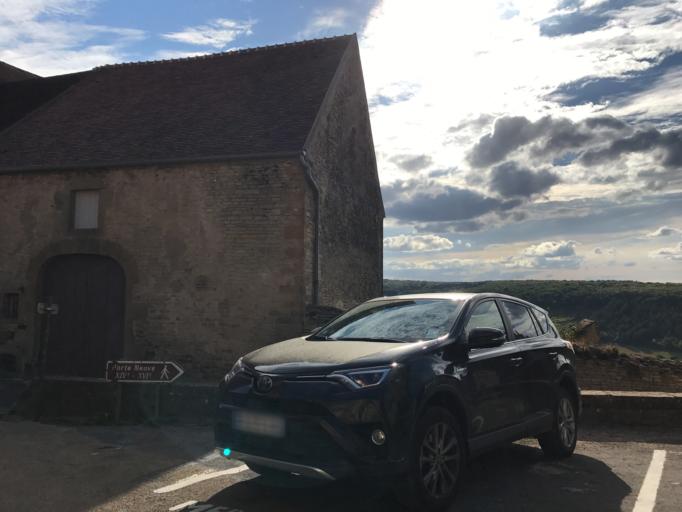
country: FR
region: Bourgogne
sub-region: Departement de l'Yonne
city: Avallon
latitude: 47.4654
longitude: 3.7448
